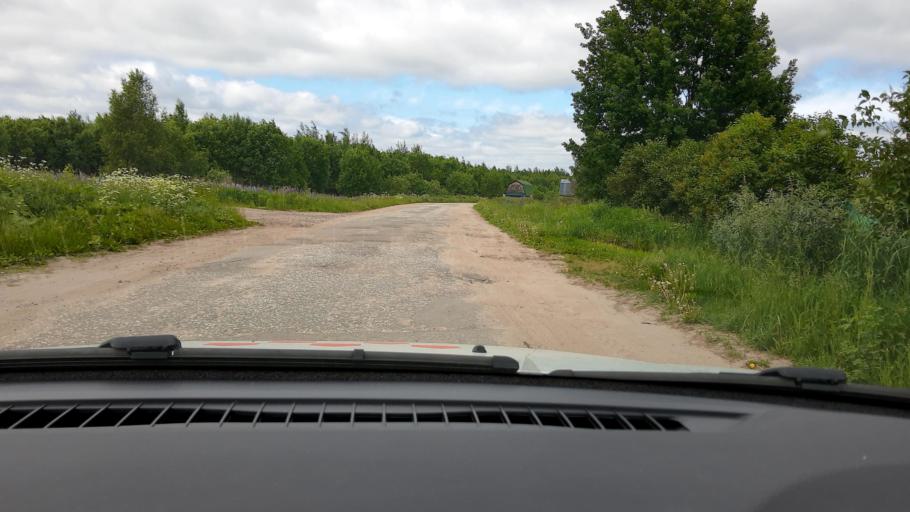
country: RU
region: Nizjnij Novgorod
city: Sitniki
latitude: 56.5196
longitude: 44.1074
